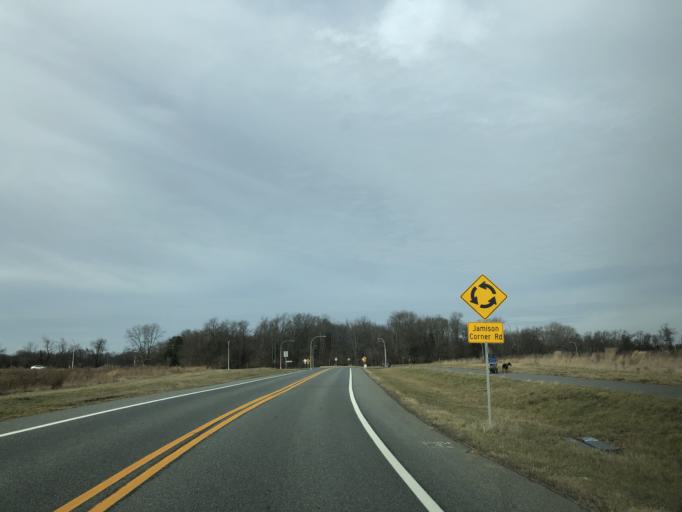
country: US
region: Delaware
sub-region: New Castle County
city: Middletown
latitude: 39.5264
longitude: -75.6772
